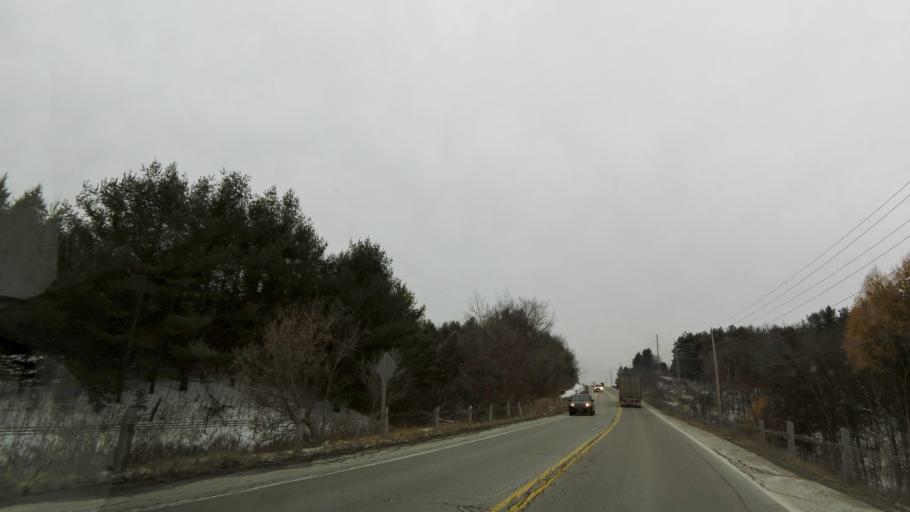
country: CA
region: Ontario
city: Vaughan
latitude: 43.9118
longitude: -79.6069
